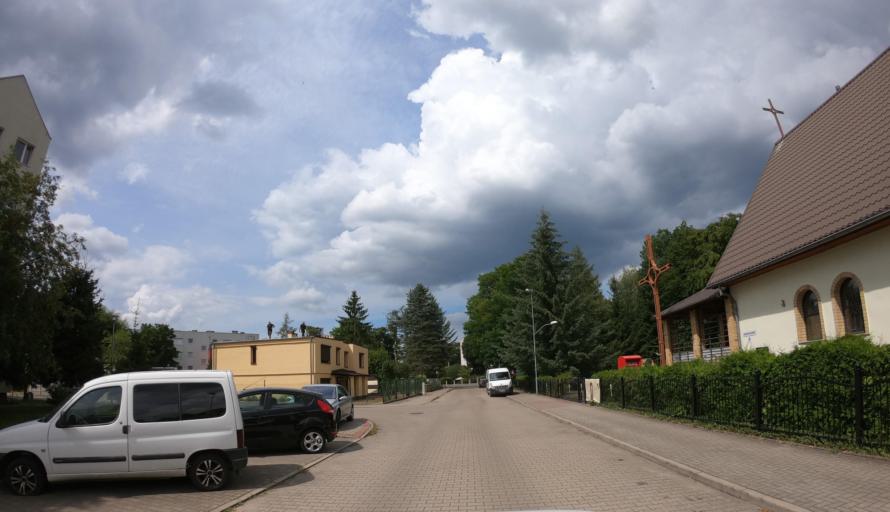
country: PL
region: West Pomeranian Voivodeship
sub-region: Powiat gryfinski
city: Stare Czarnowo
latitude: 53.3585
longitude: 14.7469
